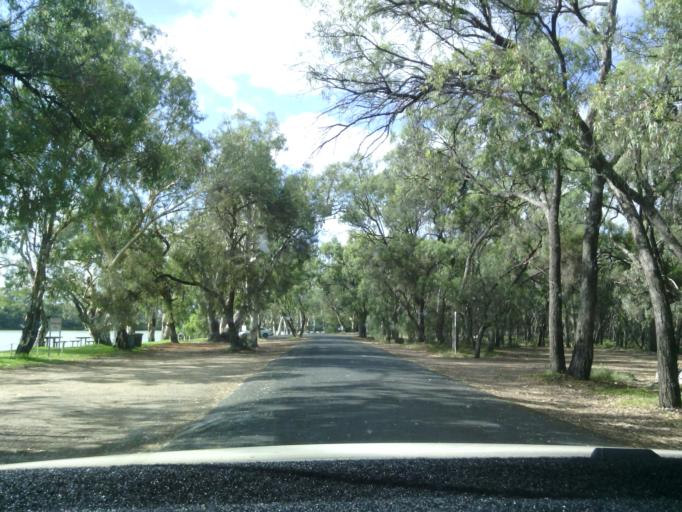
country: AU
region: South Australia
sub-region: Berri and Barmera
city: Berri
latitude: -34.2867
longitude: 140.6315
